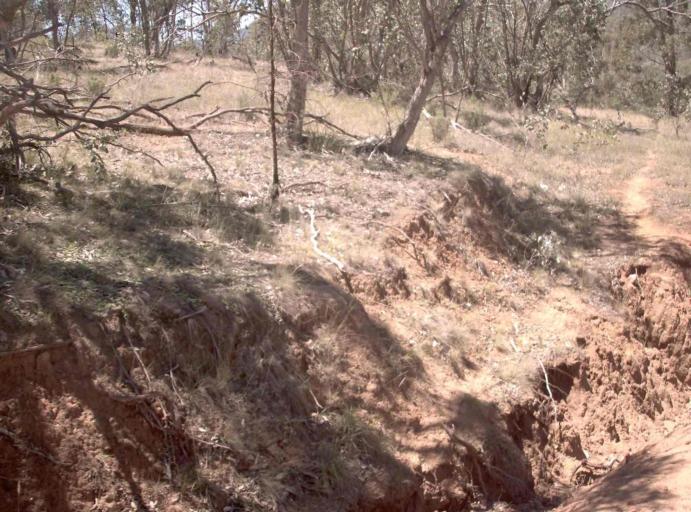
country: AU
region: New South Wales
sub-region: Snowy River
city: Jindabyne
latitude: -36.9196
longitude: 148.3990
